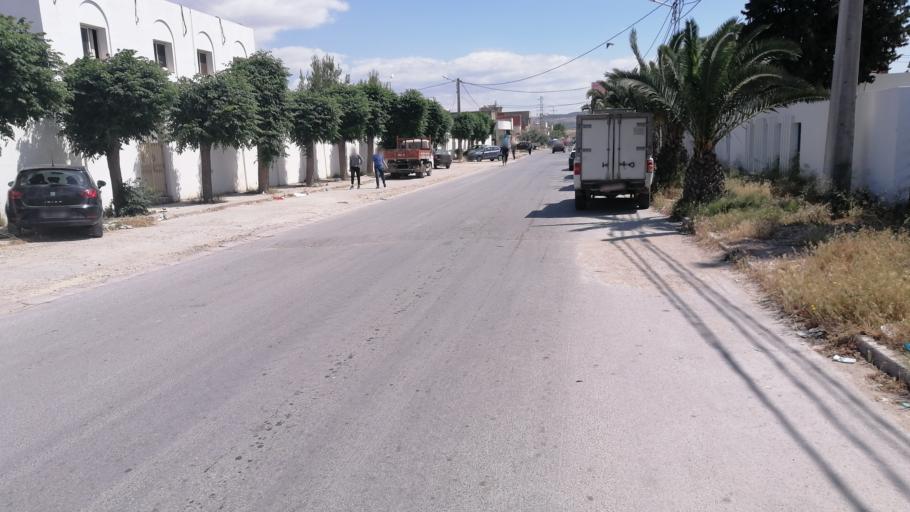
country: TN
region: Silyanah
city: Siliana
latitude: 36.0883
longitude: 9.3754
